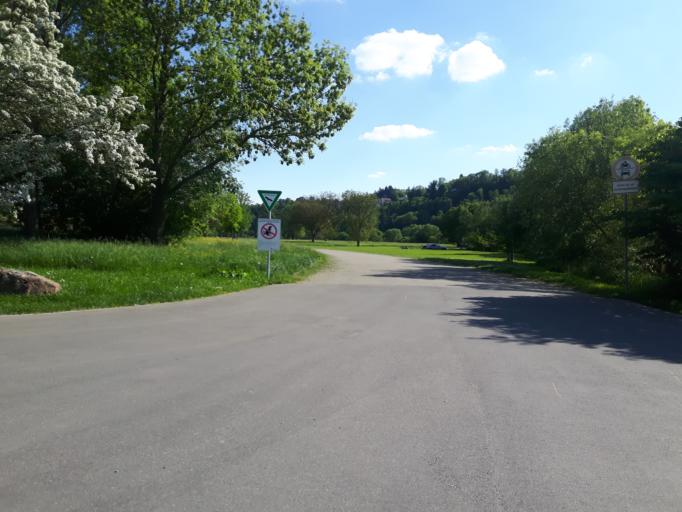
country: DE
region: Baden-Wuerttemberg
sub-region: Regierungsbezirk Stuttgart
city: Offenau
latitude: 49.2441
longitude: 9.1591
